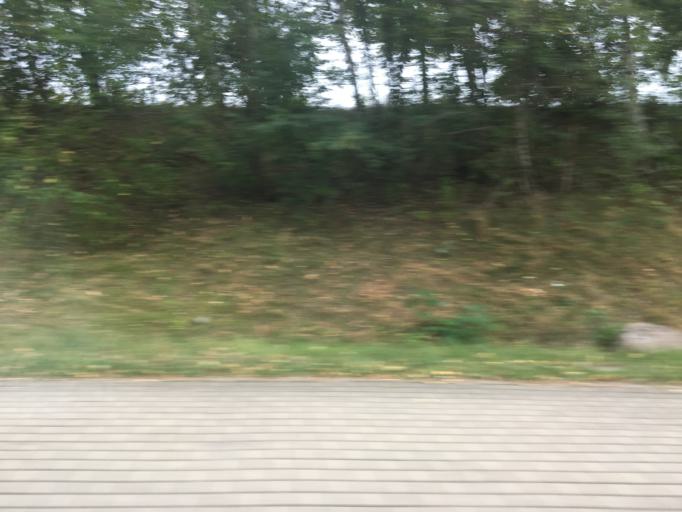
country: DE
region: Saxony
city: Wilsdruff
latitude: 51.0586
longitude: 13.5367
